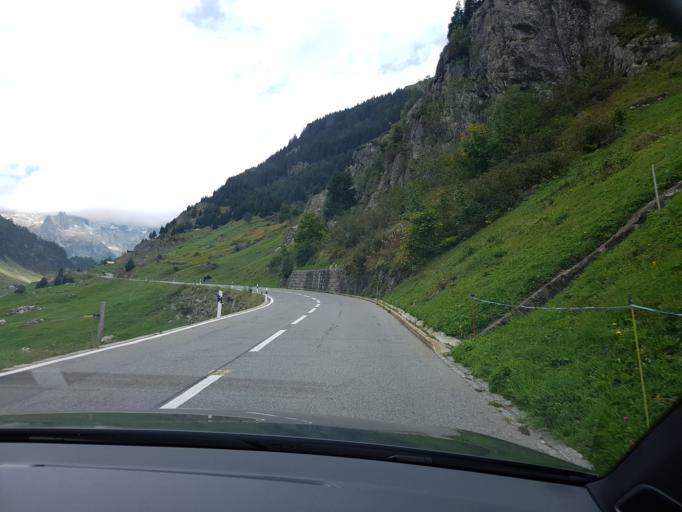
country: CH
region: Uri
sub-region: Uri
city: Andermatt
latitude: 46.7327
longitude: 8.5395
